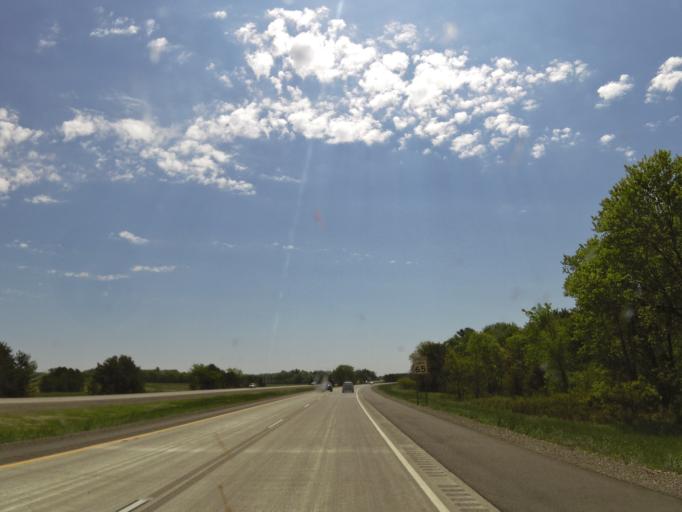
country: US
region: Wisconsin
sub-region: Jackson County
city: Black River Falls
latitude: 44.3823
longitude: -90.9933
